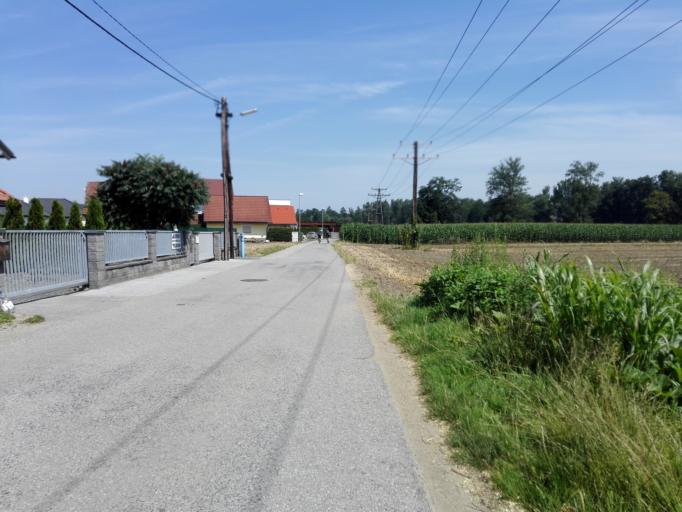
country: AT
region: Styria
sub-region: Politischer Bezirk Graz-Umgebung
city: Kalsdorf bei Graz
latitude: 46.9661
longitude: 15.4821
